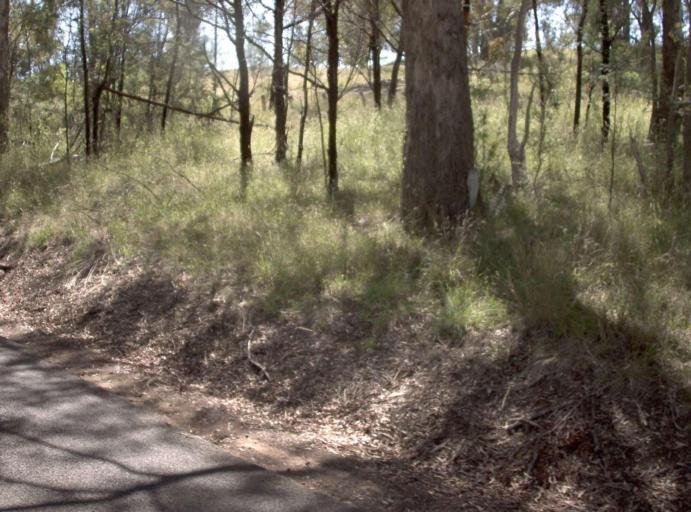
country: AU
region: Victoria
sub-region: East Gippsland
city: Lakes Entrance
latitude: -37.4358
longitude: 148.1951
